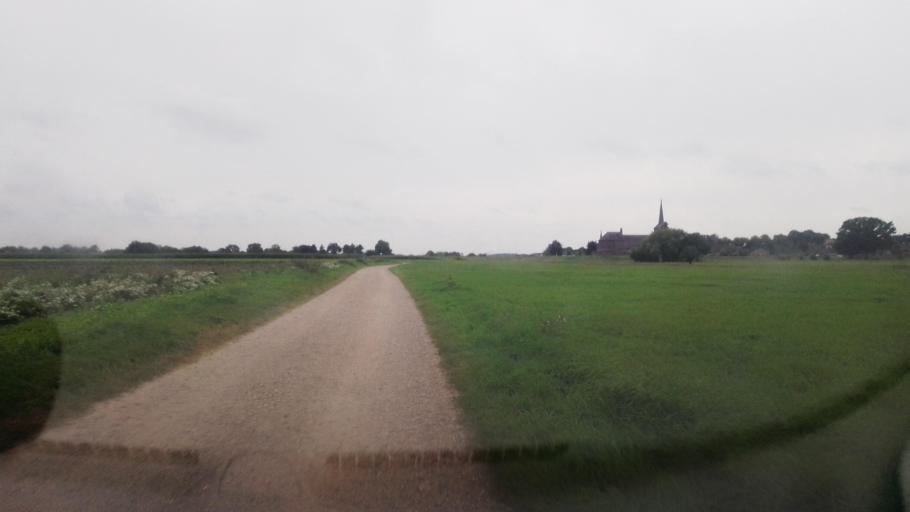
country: NL
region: Limburg
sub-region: Gemeente Venlo
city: Venlo
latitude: 51.4245
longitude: 6.1523
